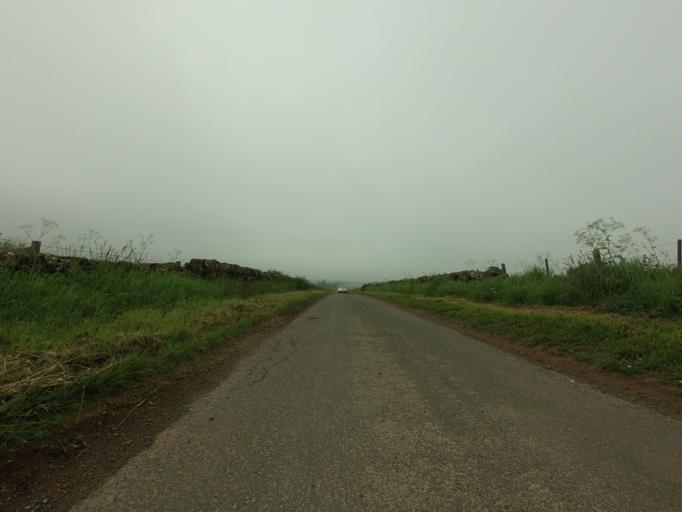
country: GB
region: Scotland
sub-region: Perth and Kinross
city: Abernethy
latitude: 56.2555
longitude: -3.3238
